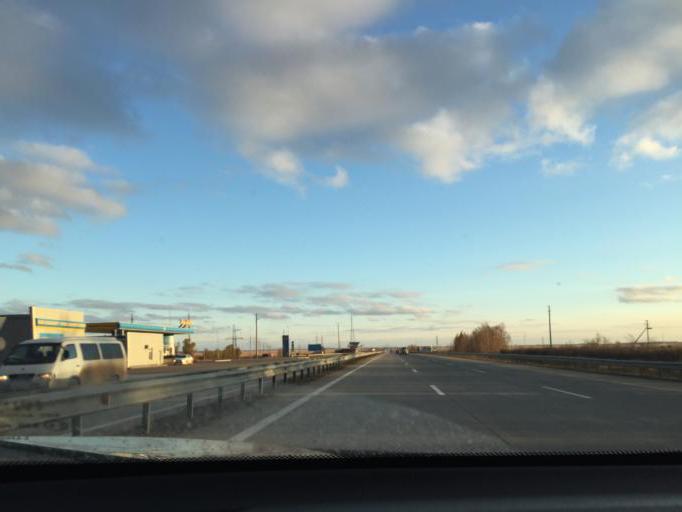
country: KZ
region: Astana Qalasy
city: Astana
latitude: 51.3086
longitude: 71.3524
